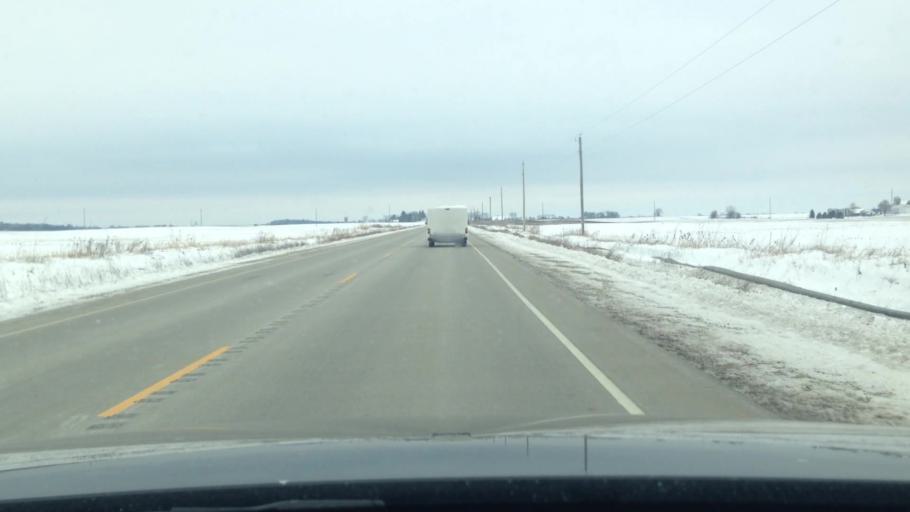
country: US
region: Illinois
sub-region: McHenry County
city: Hebron
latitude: 42.5096
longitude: -88.4426
